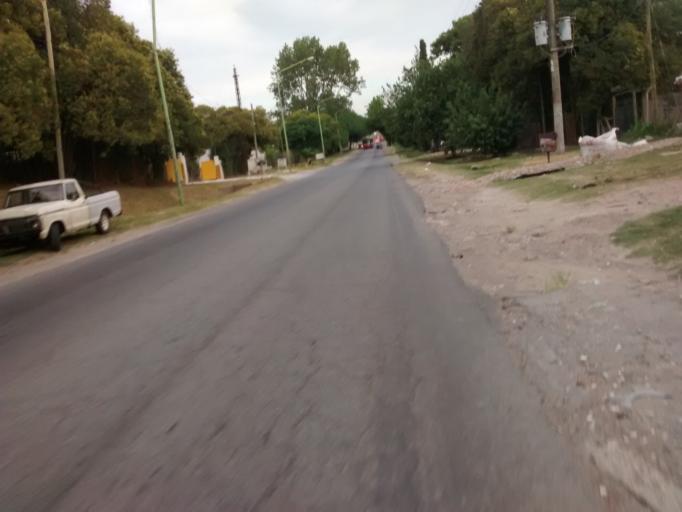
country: AR
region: Buenos Aires
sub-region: Partido de La Plata
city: La Plata
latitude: -34.9107
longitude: -58.0101
